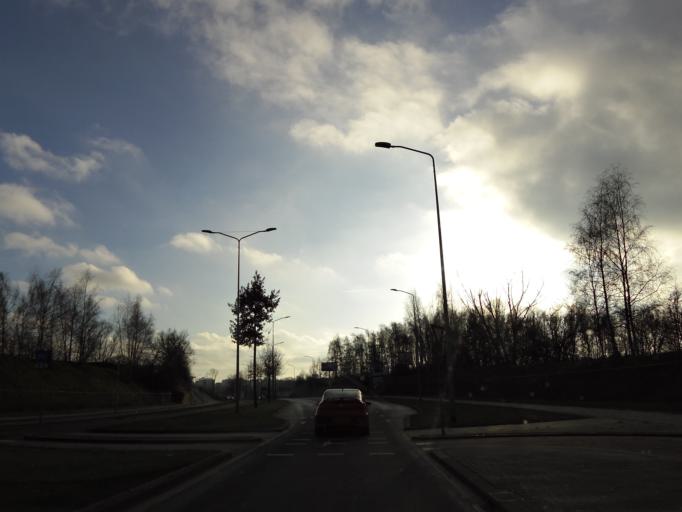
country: NL
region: Limburg
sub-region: Gemeente Heerlen
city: Heerlen
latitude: 50.9058
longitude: 5.9711
